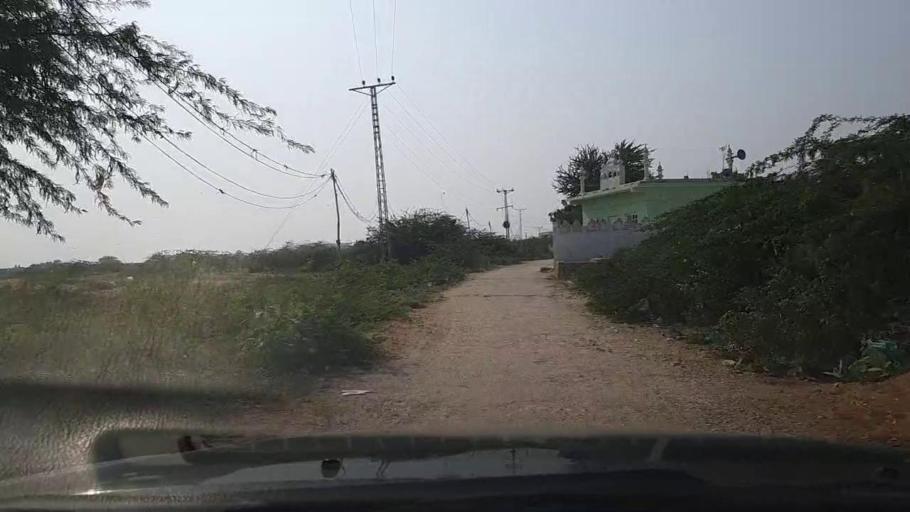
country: PK
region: Sindh
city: Thatta
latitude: 24.7413
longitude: 67.8997
